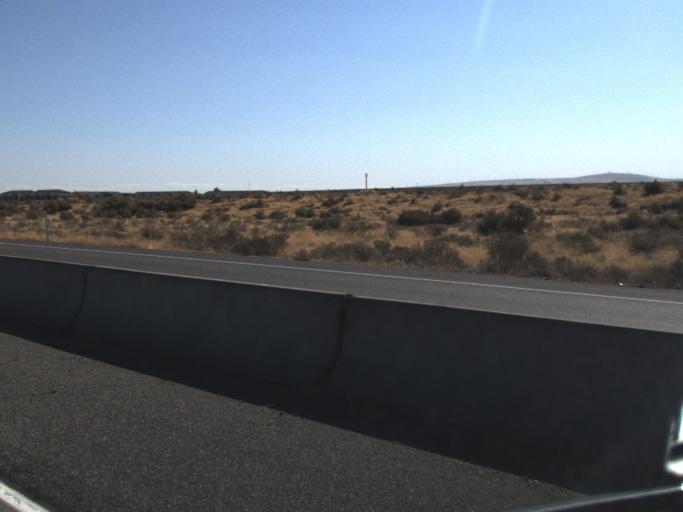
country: US
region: Washington
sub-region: Franklin County
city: West Pasco
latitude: 46.2652
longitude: -119.1814
